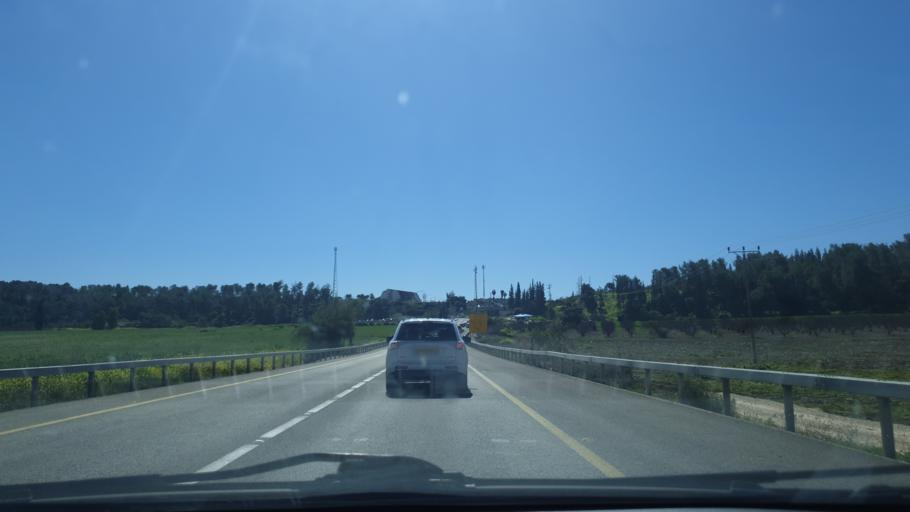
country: IL
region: Jerusalem
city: Bet Shemesh
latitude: 31.6908
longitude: 34.9442
